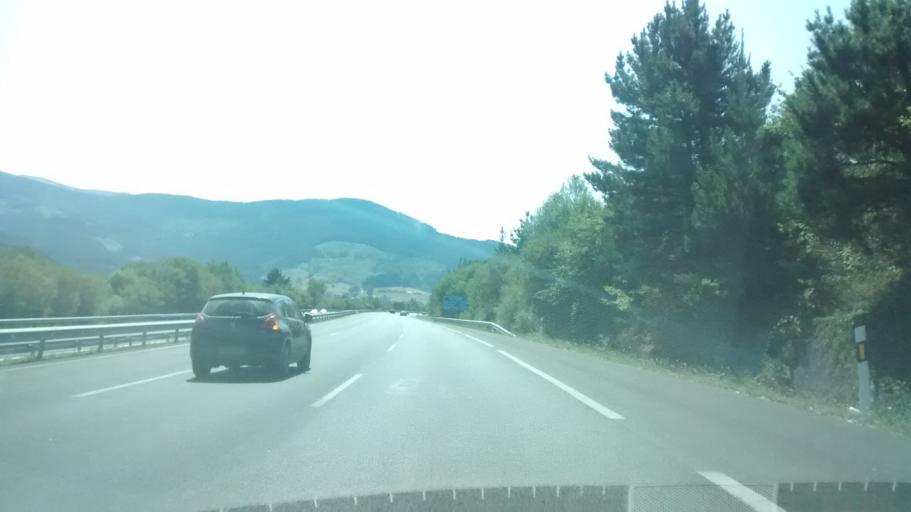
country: ES
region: Basque Country
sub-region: Bizkaia
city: Elexalde
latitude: 43.1179
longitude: -2.9158
